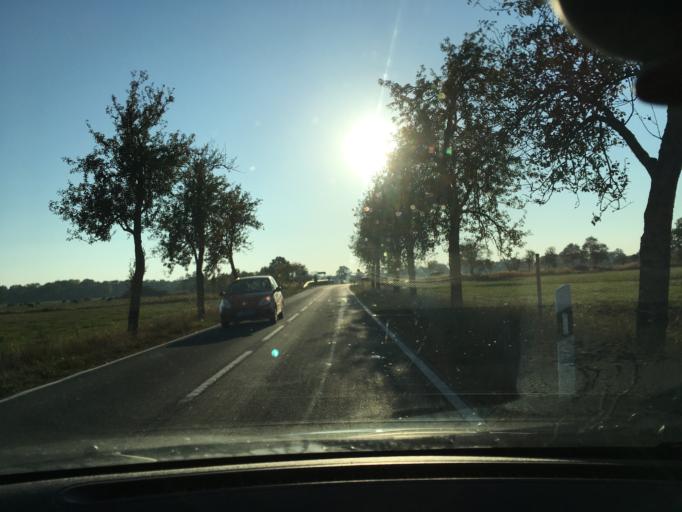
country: DE
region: Lower Saxony
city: Neu Darchau
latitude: 53.2884
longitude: 10.8491
